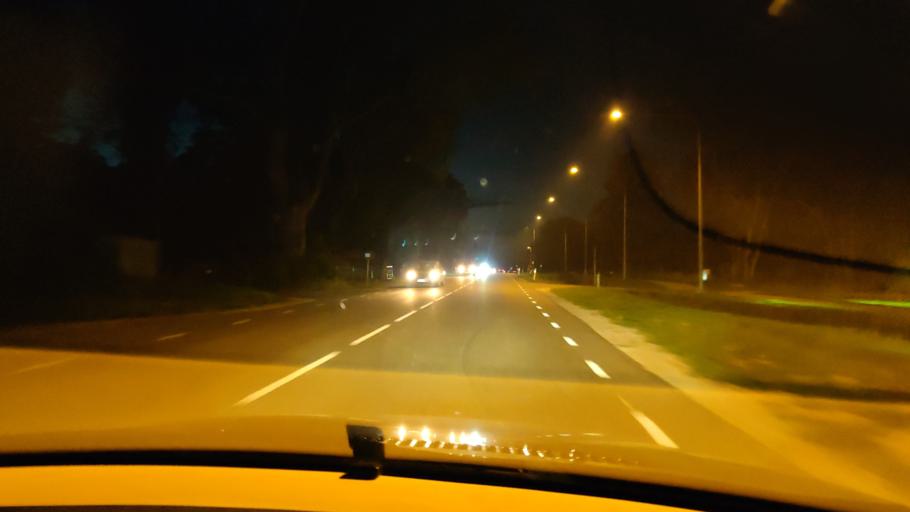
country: EE
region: Harju
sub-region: Paldiski linn
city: Paldiski
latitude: 59.3784
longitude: 24.2381
